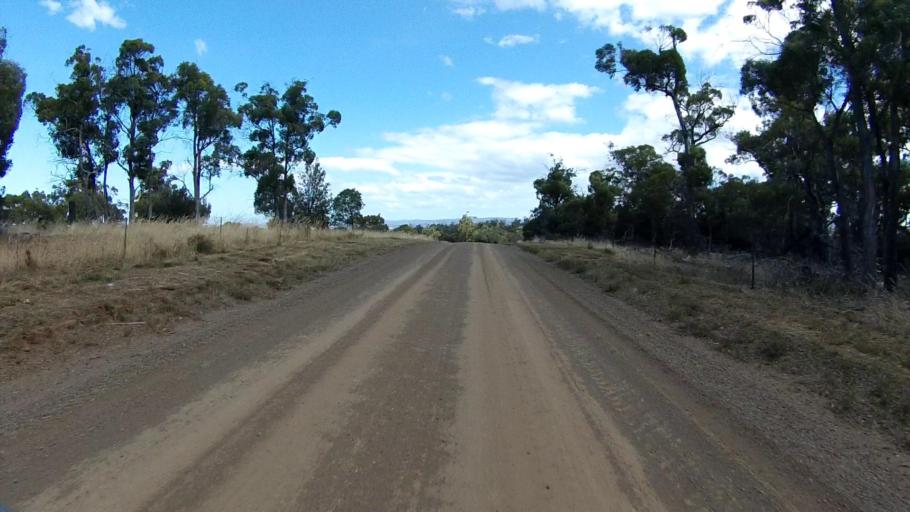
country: AU
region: Tasmania
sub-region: Break O'Day
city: St Helens
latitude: -41.9806
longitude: 148.0668
